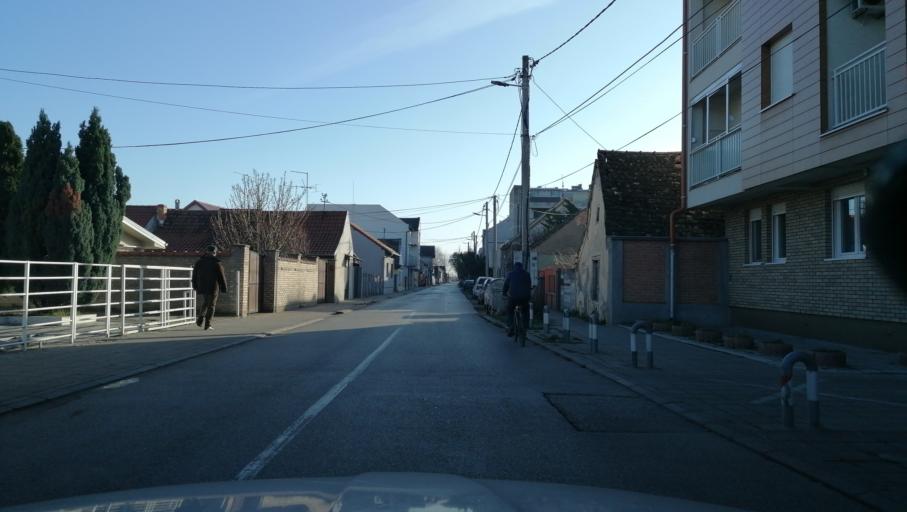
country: RS
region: Autonomna Pokrajina Vojvodina
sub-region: Sremski Okrug
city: Sremska Mitrovica
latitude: 44.9665
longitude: 19.6123
